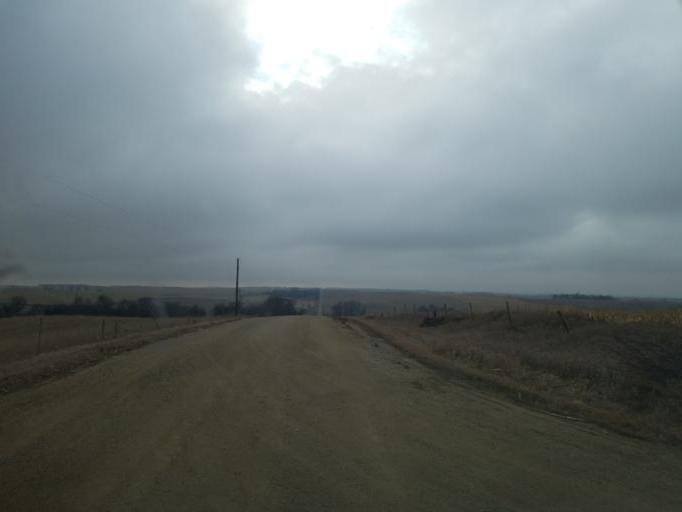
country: US
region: Nebraska
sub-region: Knox County
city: Creighton
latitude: 42.4957
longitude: -97.7984
